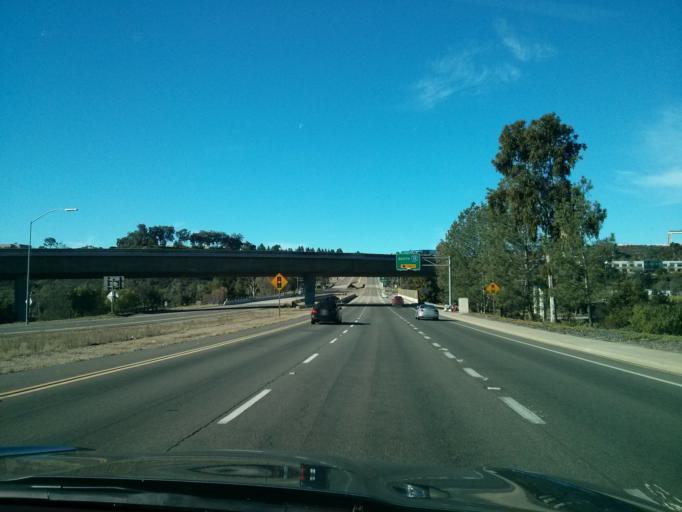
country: US
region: California
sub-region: San Diego County
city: La Mesa
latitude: 32.8232
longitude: -117.1145
